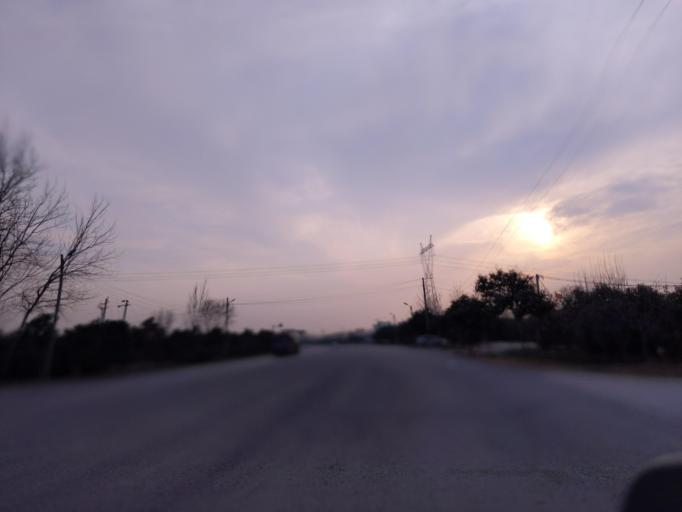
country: CN
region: Henan Sheng
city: Puyang
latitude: 35.8184
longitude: 114.9716
